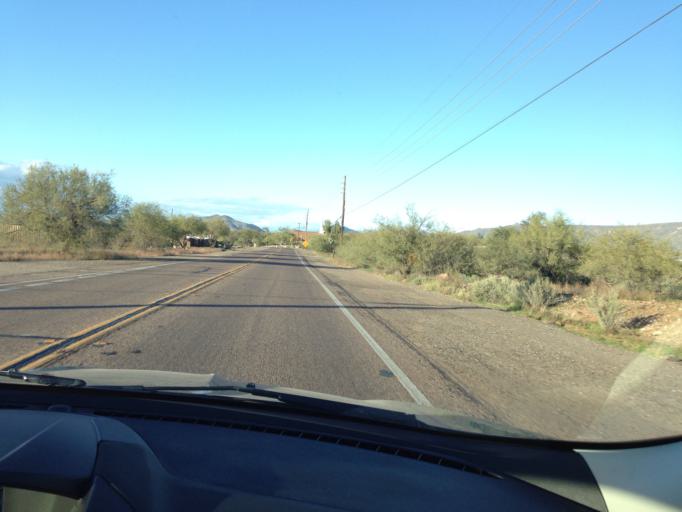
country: US
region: Arizona
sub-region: Maricopa County
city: New River
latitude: 33.8876
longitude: -112.0728
